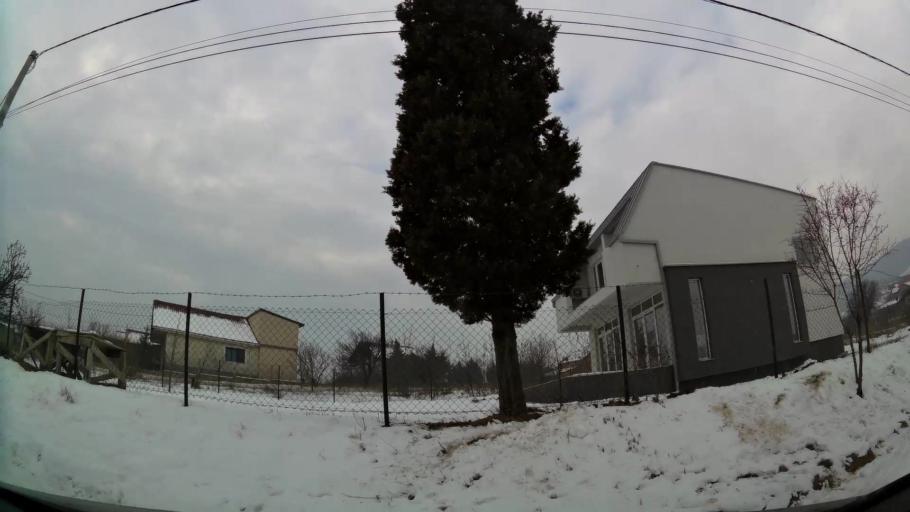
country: MK
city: Kondovo
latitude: 42.0424
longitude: 21.3433
